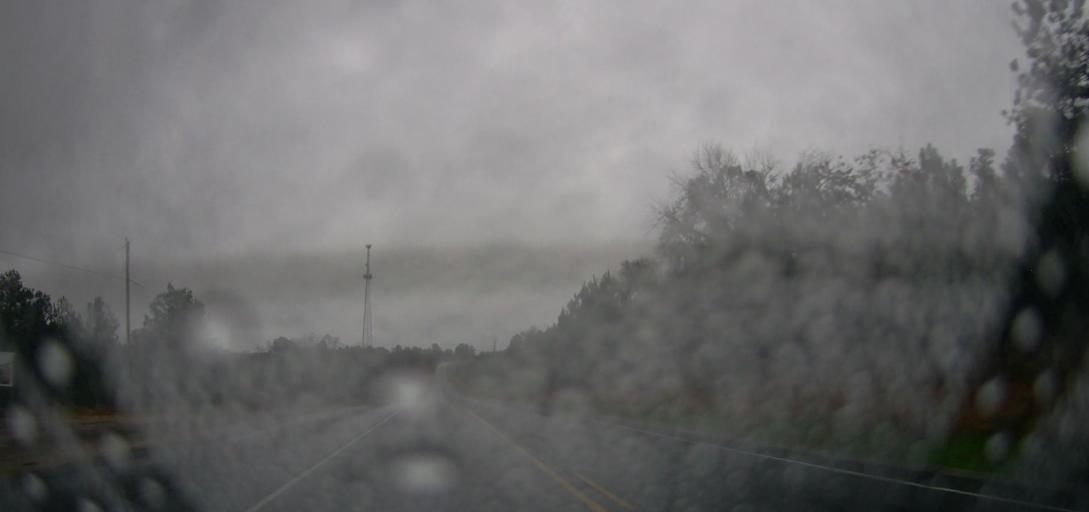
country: US
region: Alabama
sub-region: Chilton County
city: Clanton
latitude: 32.6443
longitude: -86.7595
